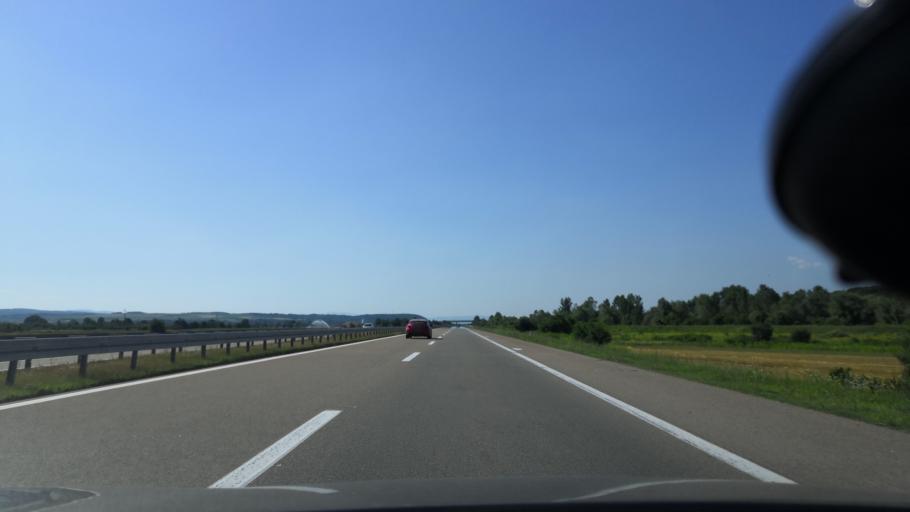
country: RS
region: Central Serbia
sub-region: Jablanicki Okrug
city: Leskovac
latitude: 43.0506
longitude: 21.9825
